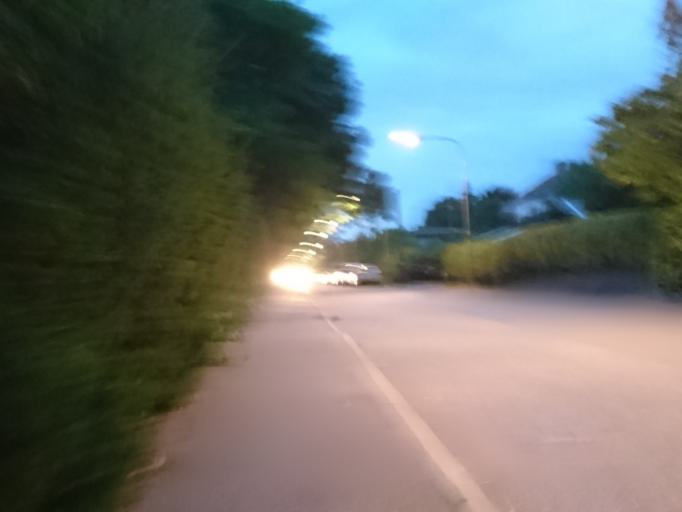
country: SE
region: Stockholm
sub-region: Huddinge Kommun
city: Huddinge
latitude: 59.2751
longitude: 17.9946
